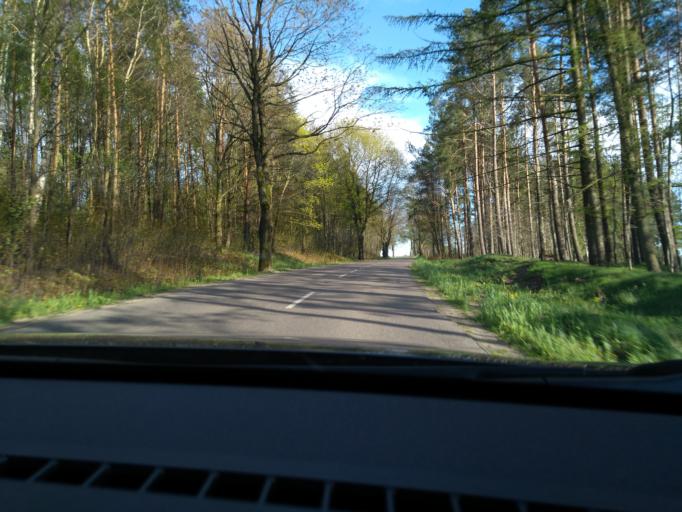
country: PL
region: Pomeranian Voivodeship
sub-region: Powiat kartuski
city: Suleczyno
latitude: 54.3303
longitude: 17.7746
